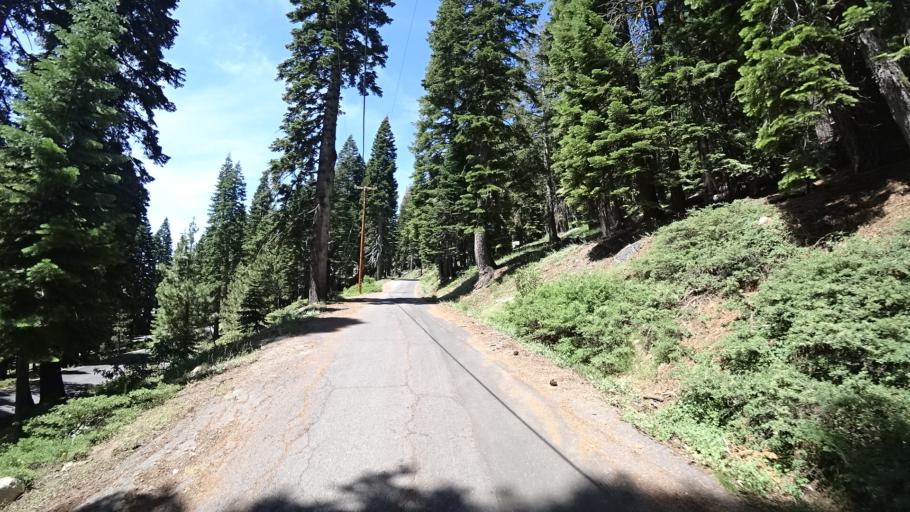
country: US
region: California
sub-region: Calaveras County
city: Arnold
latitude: 38.4293
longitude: -120.0942
